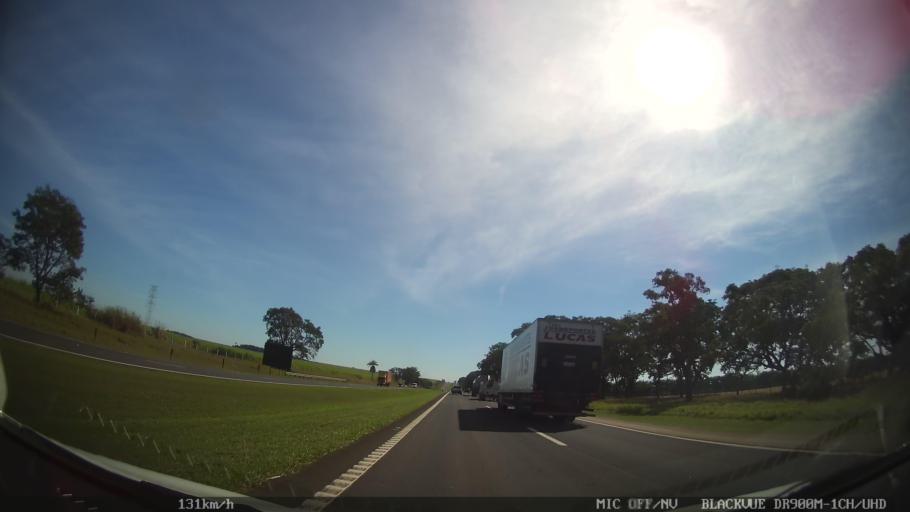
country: BR
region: Sao Paulo
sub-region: Porto Ferreira
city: Porto Ferreira
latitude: -21.8985
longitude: -47.4797
